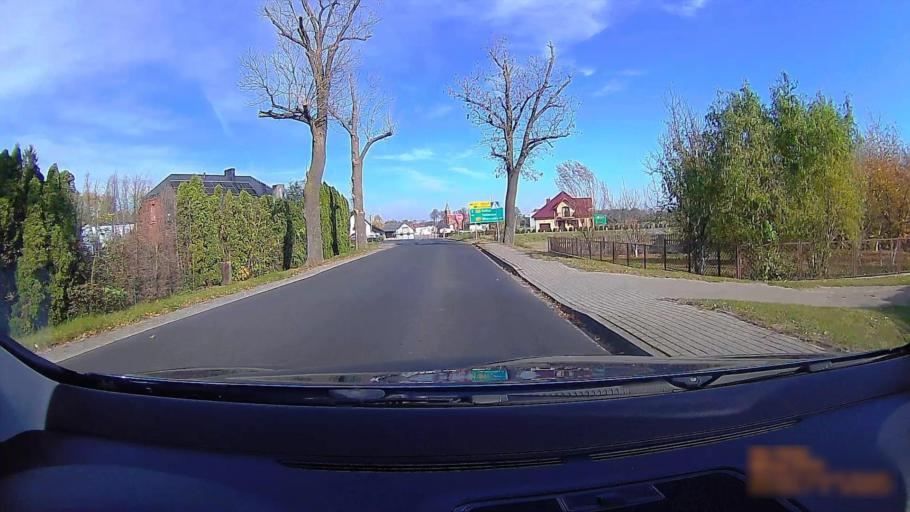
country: PL
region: Greater Poland Voivodeship
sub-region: Powiat ostrzeszowski
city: Doruchow
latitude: 51.4115
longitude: 18.0759
